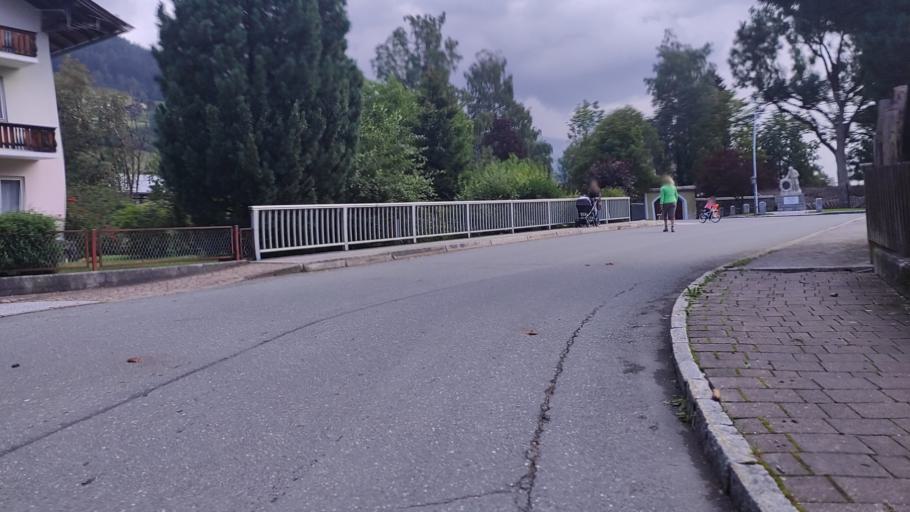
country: AT
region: Salzburg
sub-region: Politischer Bezirk Zell am See
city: Bramberg am Wildkogel
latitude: 47.2780
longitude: 12.3753
